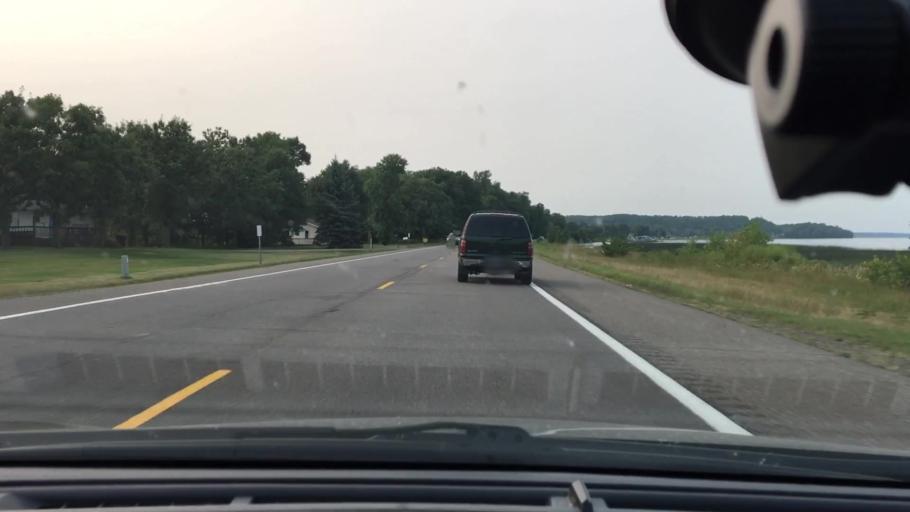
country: US
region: Minnesota
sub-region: Mille Lacs County
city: Vineland
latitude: 46.2592
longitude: -93.8236
